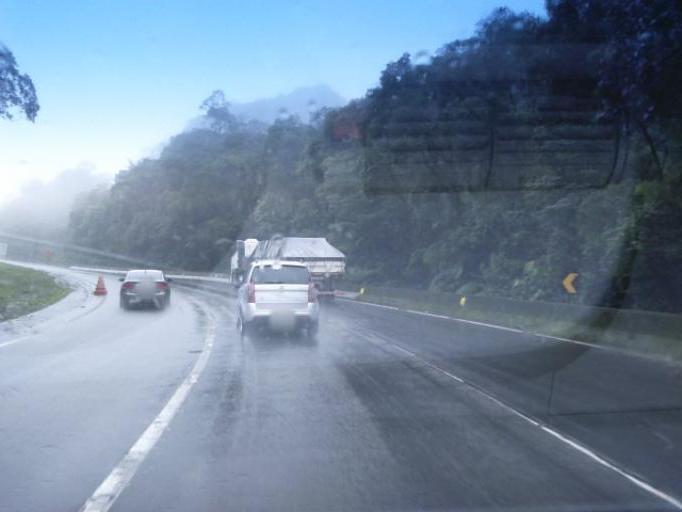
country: BR
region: Parana
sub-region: Guaratuba
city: Guaratuba
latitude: -25.8543
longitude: -48.9505
